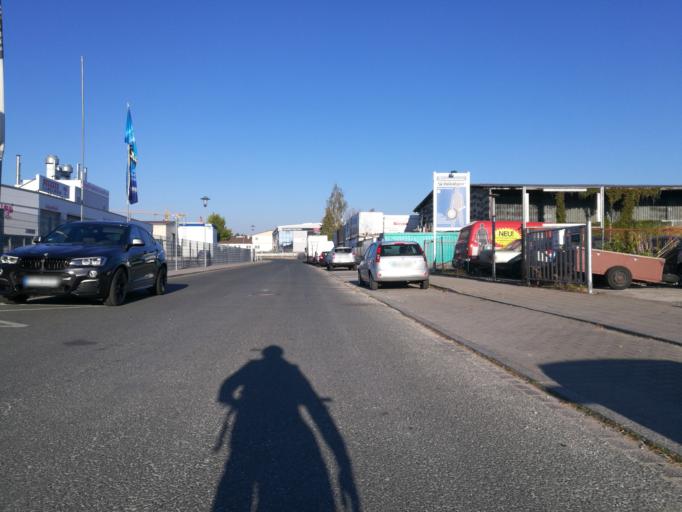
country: DE
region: Bavaria
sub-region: Regierungsbezirk Mittelfranken
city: Veitsbronn
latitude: 49.4926
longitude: 10.9230
